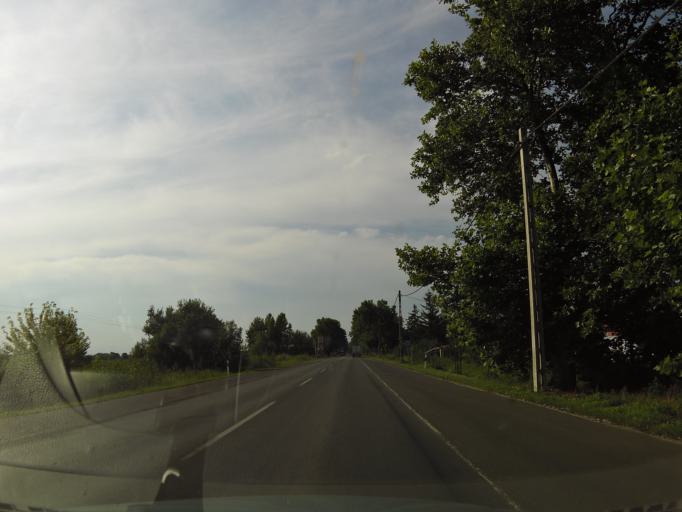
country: HU
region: Csongrad
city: Balastya
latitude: 46.4129
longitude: 20.0193
